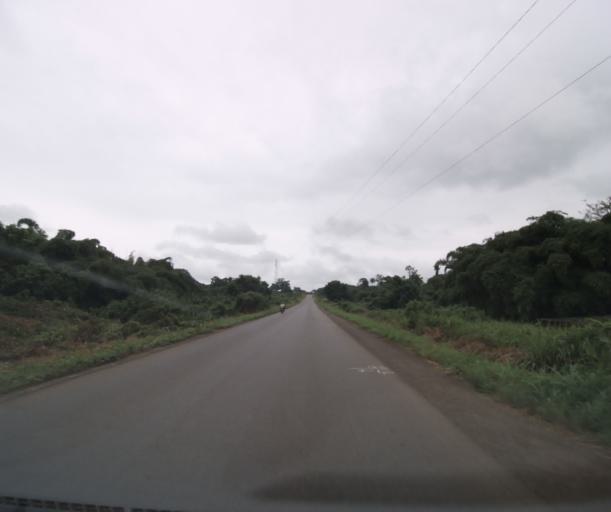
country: CM
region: Littoral
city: Edea
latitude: 3.7319
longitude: 10.1136
